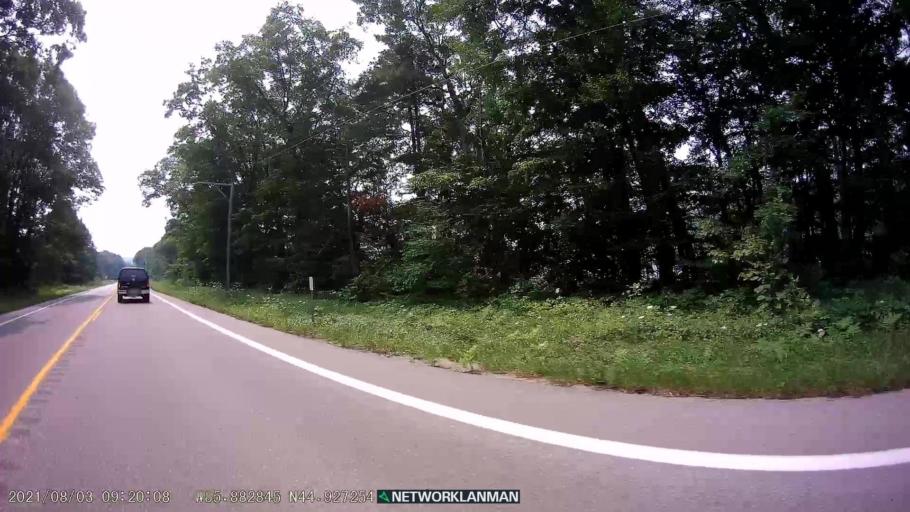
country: US
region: Michigan
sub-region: Leelanau County
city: Leland
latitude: 44.9271
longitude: -85.8827
